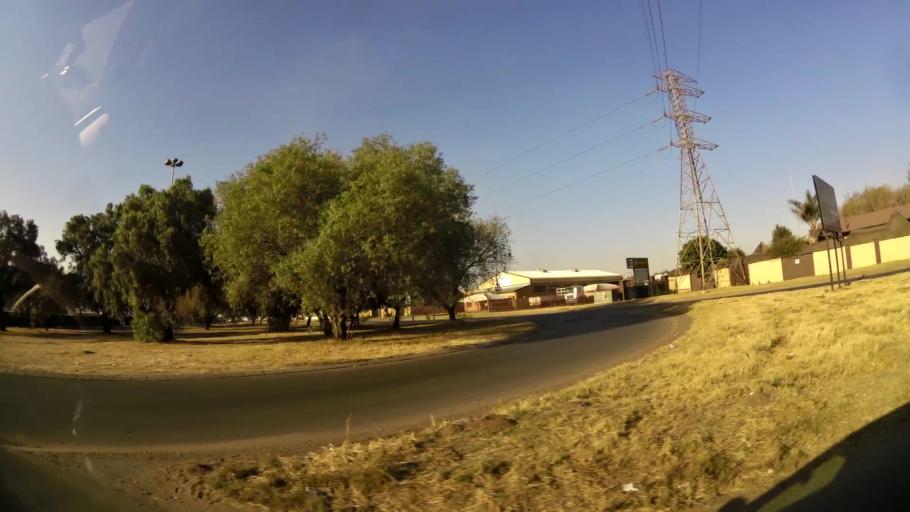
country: ZA
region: Gauteng
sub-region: West Rand District Municipality
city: Randfontein
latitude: -26.1930
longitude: 27.6919
